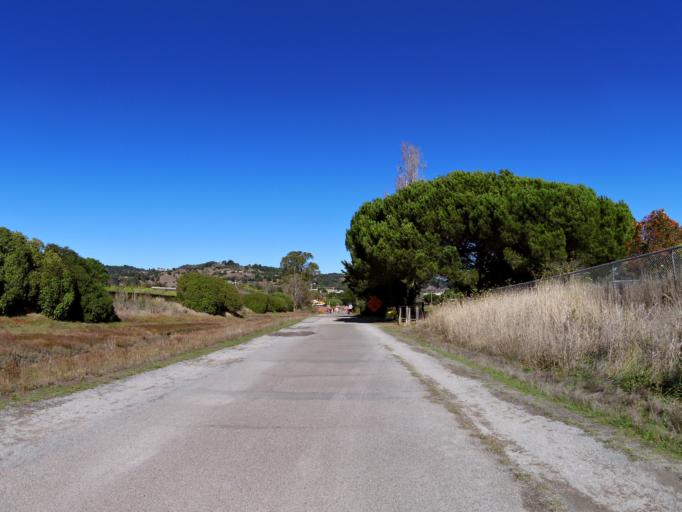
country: US
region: California
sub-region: Marin County
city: Strawberry
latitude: 37.8948
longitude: -122.5258
